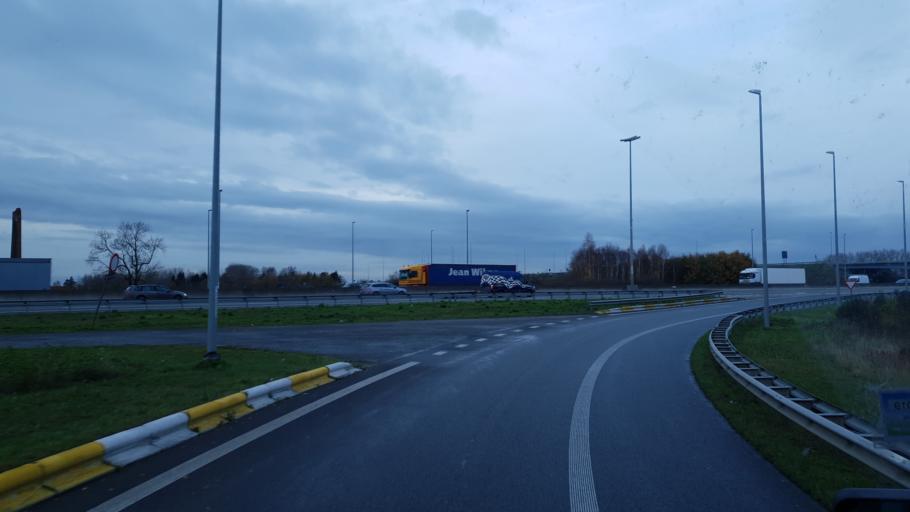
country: BE
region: Flanders
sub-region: Provincie Oost-Vlaanderen
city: Nazareth
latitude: 50.9538
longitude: 3.5621
